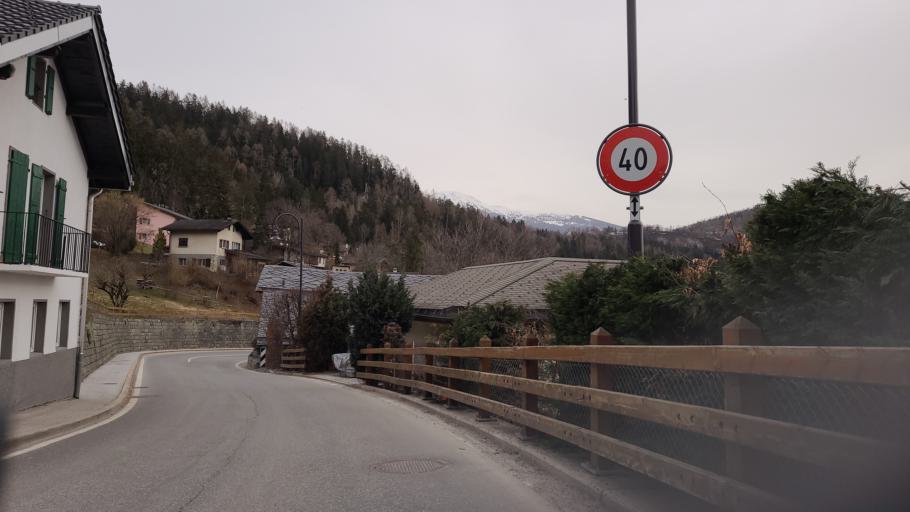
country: CH
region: Valais
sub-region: Sierre District
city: Lens
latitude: 46.2895
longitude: 7.4387
